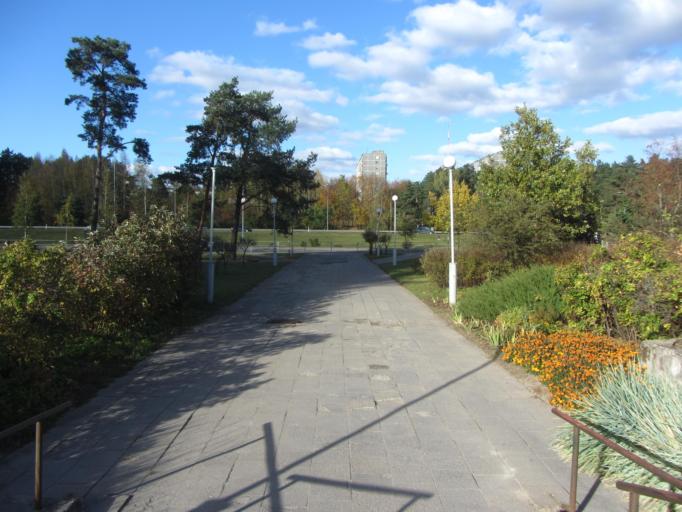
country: LT
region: Vilnius County
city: Lazdynai
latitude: 54.6692
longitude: 25.2079
